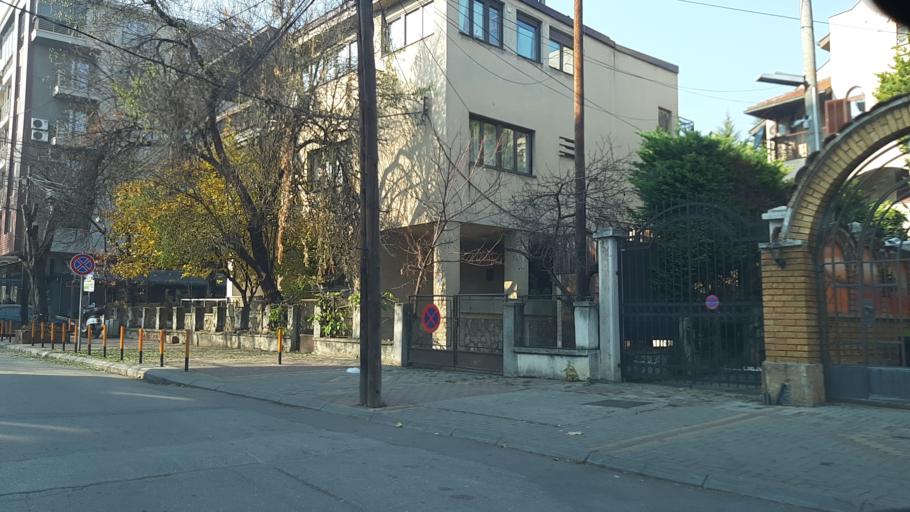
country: MK
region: Karpos
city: Skopje
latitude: 42.0007
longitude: 21.4218
